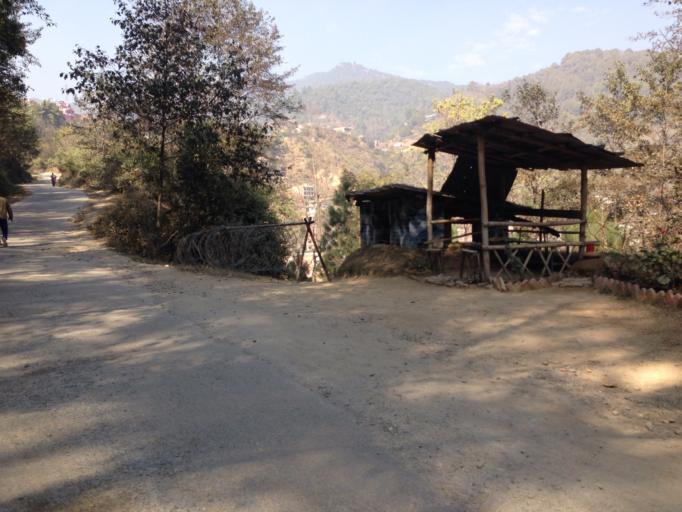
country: NP
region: Central Region
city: Kirtipur
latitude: 27.7210
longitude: 85.2769
